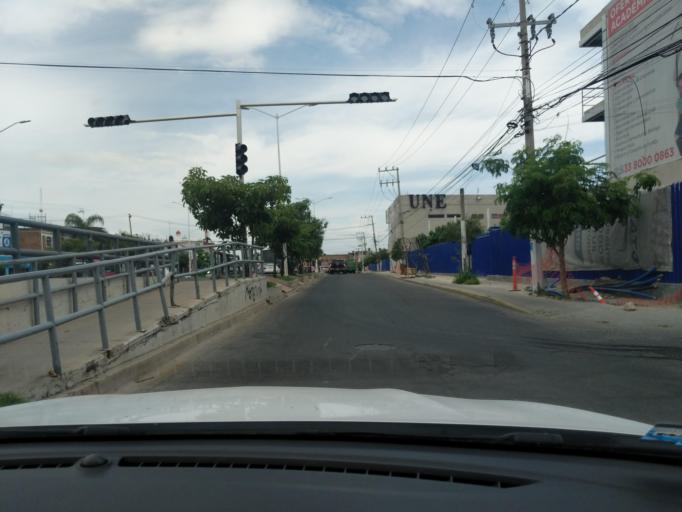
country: MX
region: Jalisco
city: Nuevo Mexico
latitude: 20.7617
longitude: -103.4386
